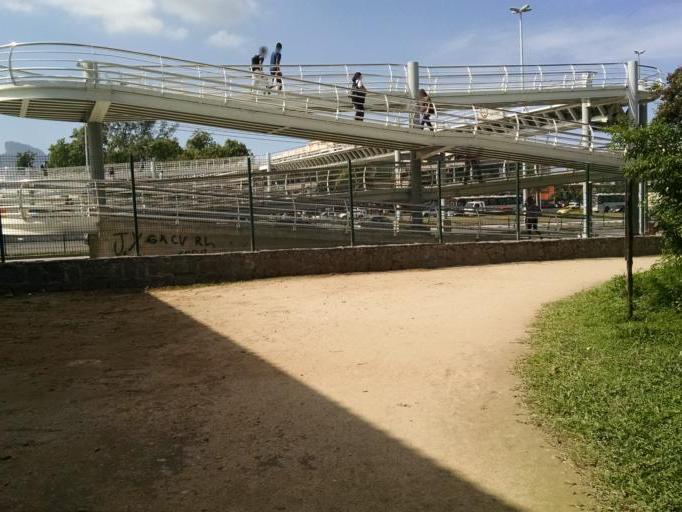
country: BR
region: Rio de Janeiro
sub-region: Rio De Janeiro
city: Rio de Janeiro
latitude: -22.9950
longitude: -43.3667
